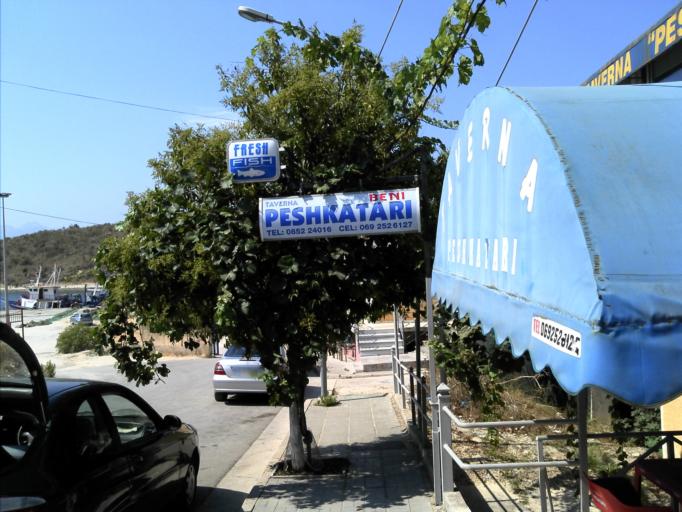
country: AL
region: Vlore
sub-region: Rrethi i Sarandes
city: Sarande
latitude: 39.8736
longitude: 19.9901
